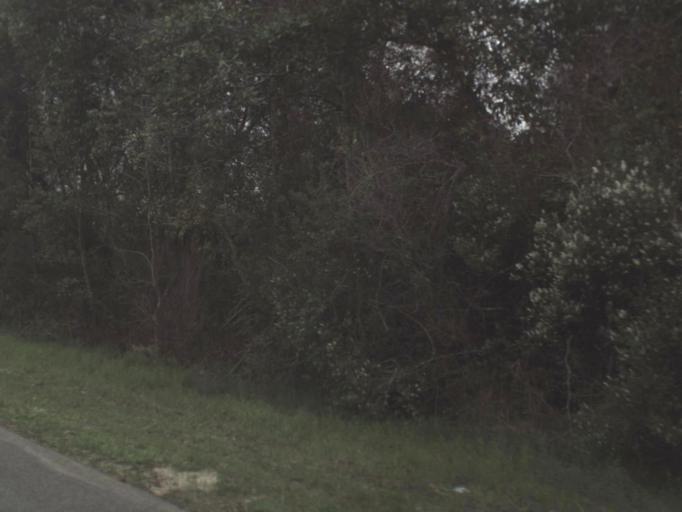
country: US
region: Florida
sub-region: Gadsden County
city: Gretna
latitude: 30.4934
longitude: -84.7197
